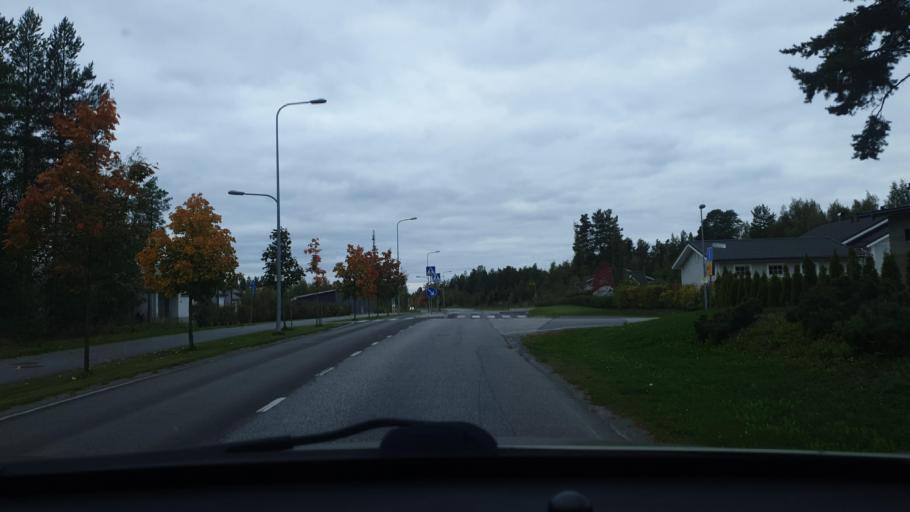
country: FI
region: Ostrobothnia
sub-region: Vaasa
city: Korsholm
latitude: 63.1043
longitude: 21.6759
